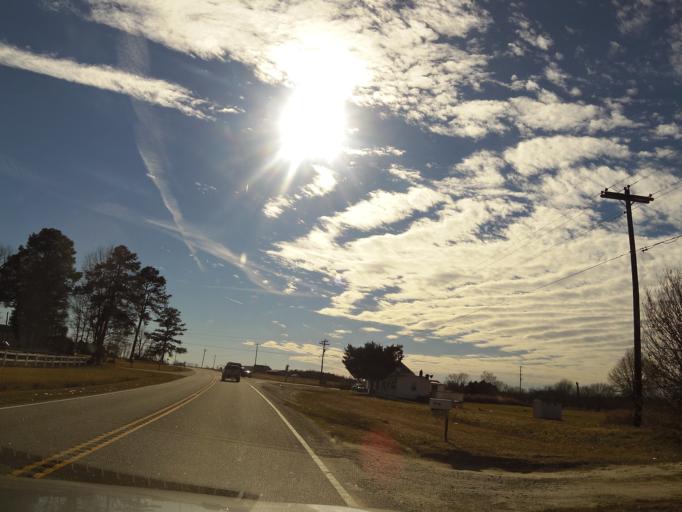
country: US
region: Virginia
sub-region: City of Franklin
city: Franklin
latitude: 36.7427
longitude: -76.8757
